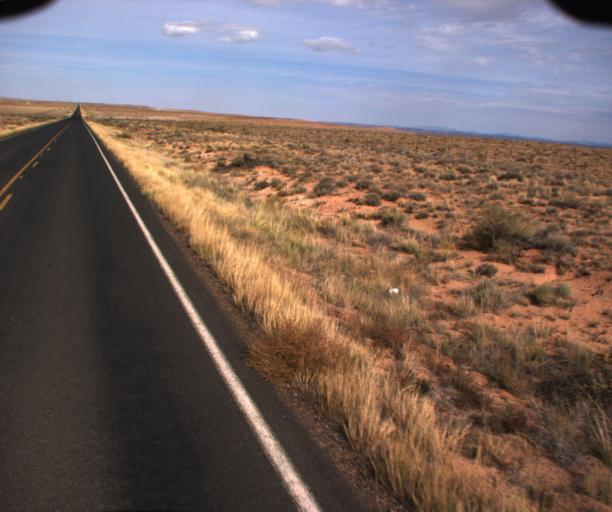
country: US
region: Arizona
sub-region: Apache County
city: Chinle
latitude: 35.9739
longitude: -109.5990
